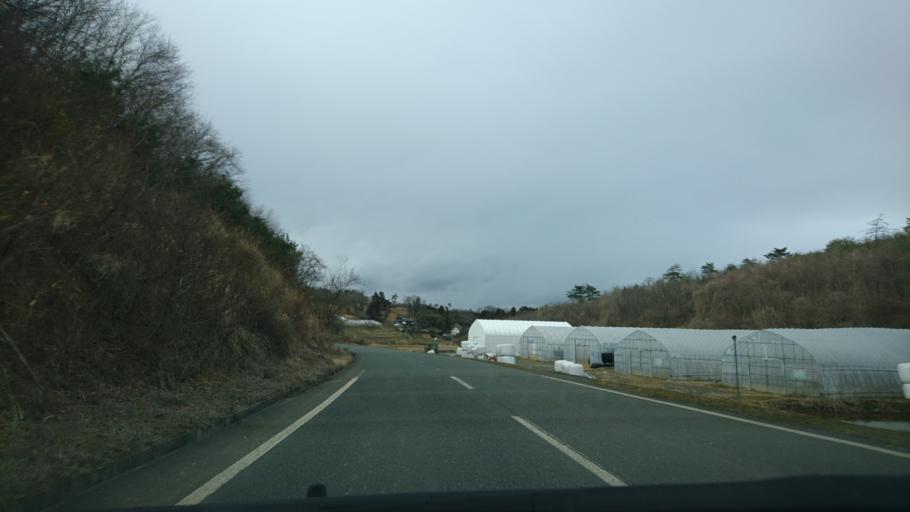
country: JP
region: Iwate
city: Ichinoseki
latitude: 38.8491
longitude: 141.2106
